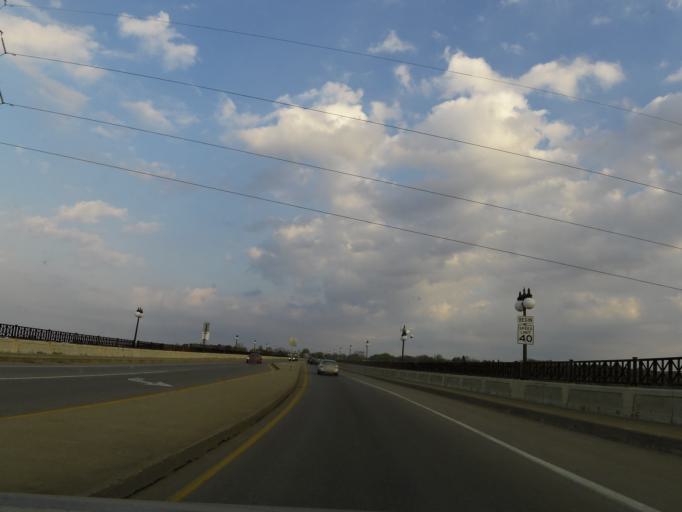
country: US
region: Minnesota
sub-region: Ramsey County
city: Saint Paul
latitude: 44.9367
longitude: -93.1087
